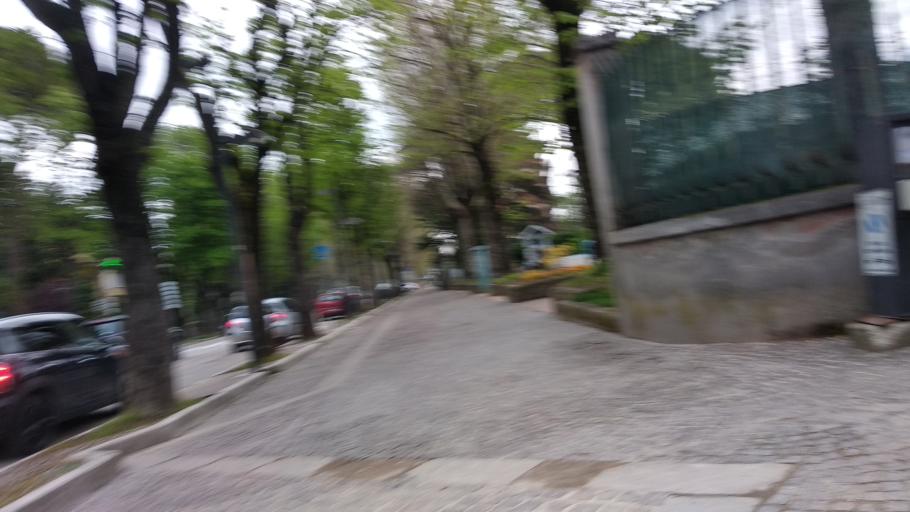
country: IT
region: Emilia-Romagna
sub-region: Forli-Cesena
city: Castrocaro Terme
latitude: 44.1737
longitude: 11.9494
